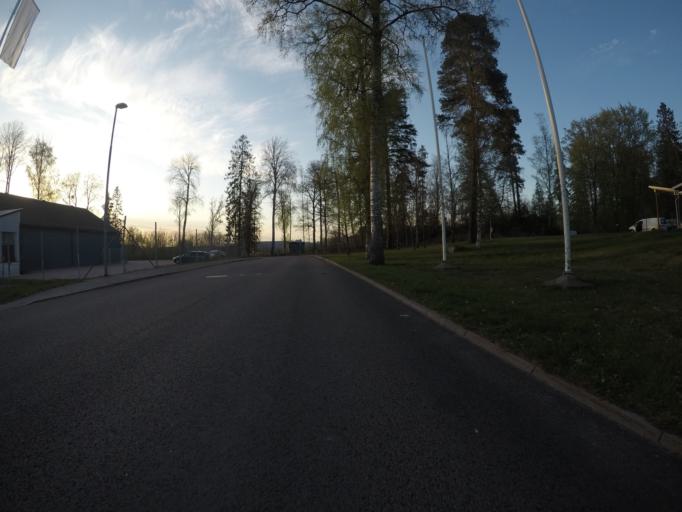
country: SE
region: Vaestmanland
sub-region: Vasteras
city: Vasteras
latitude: 59.5926
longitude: 16.6187
